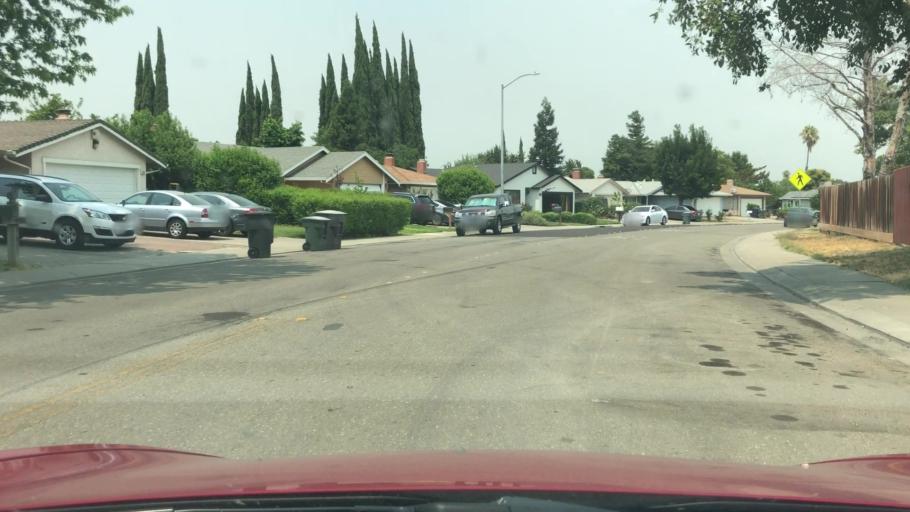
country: US
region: California
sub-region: San Joaquin County
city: Tracy
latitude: 37.7341
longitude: -121.4408
